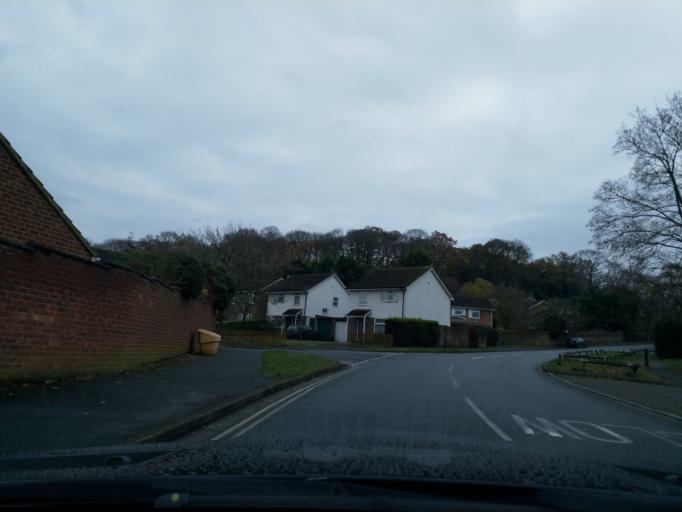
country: GB
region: England
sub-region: Surrey
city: Frimley
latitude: 51.3160
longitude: -0.7294
